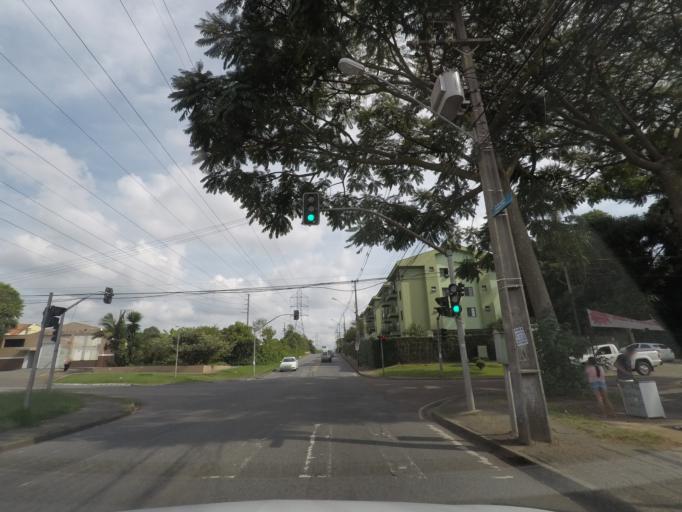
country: BR
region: Parana
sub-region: Pinhais
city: Pinhais
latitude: -25.4808
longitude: -49.2117
